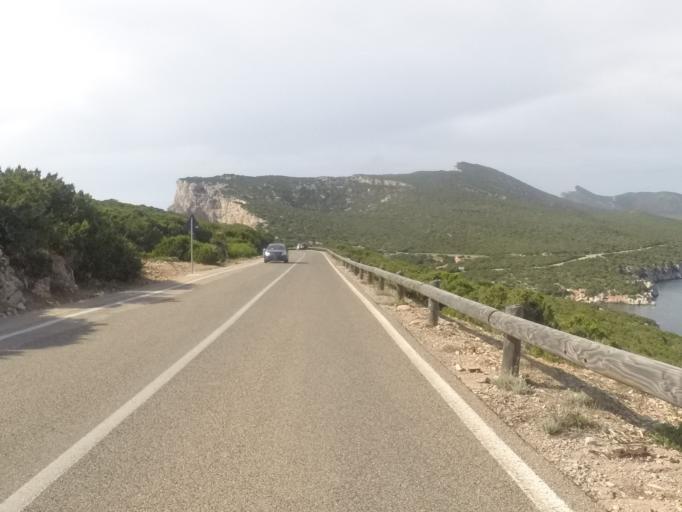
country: IT
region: Sardinia
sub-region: Provincia di Sassari
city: Alghero
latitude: 40.5723
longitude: 8.1627
